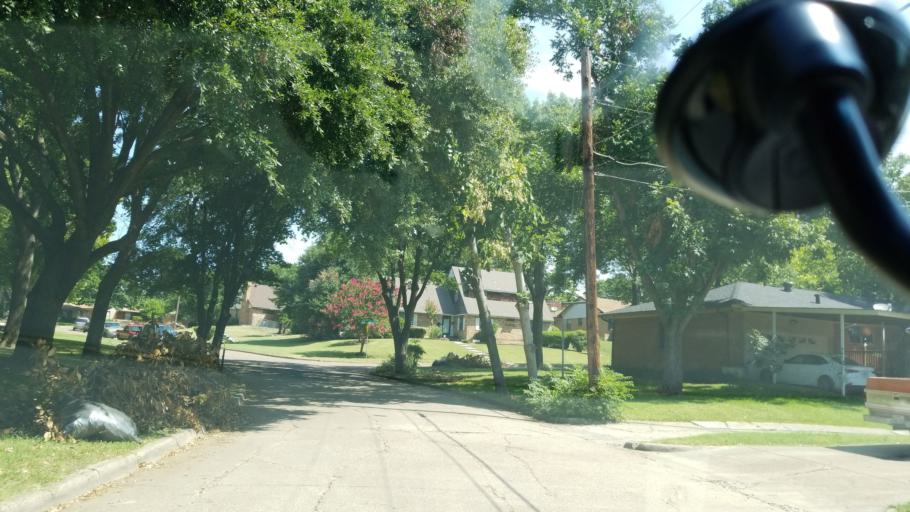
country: US
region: Texas
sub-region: Dallas County
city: Cockrell Hill
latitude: 32.7083
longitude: -96.8799
